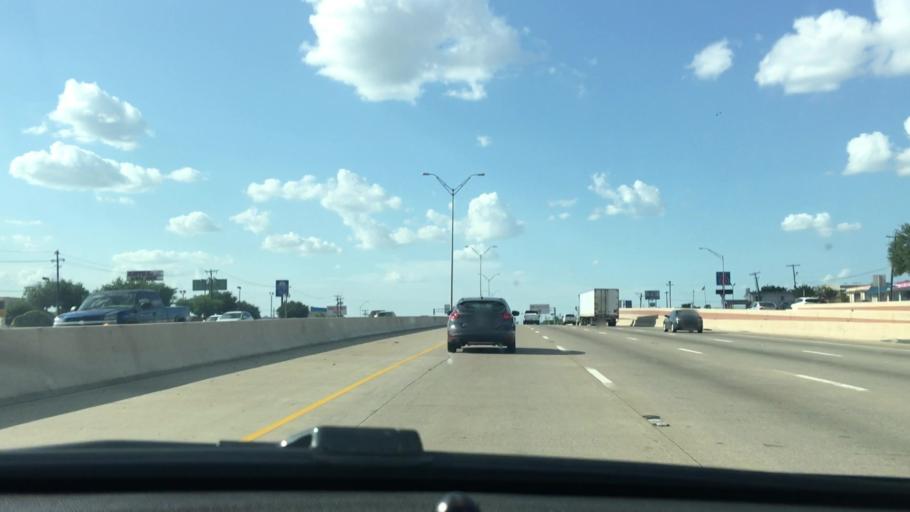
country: US
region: Texas
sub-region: Dallas County
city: DeSoto
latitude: 32.6076
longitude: -96.8229
